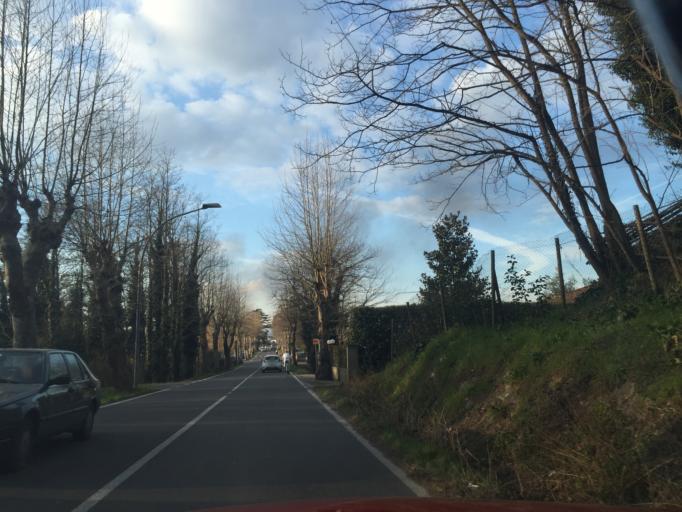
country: IT
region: Tuscany
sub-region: Provincia di Pistoia
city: Lamporecchio
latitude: 43.8191
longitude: 10.8832
